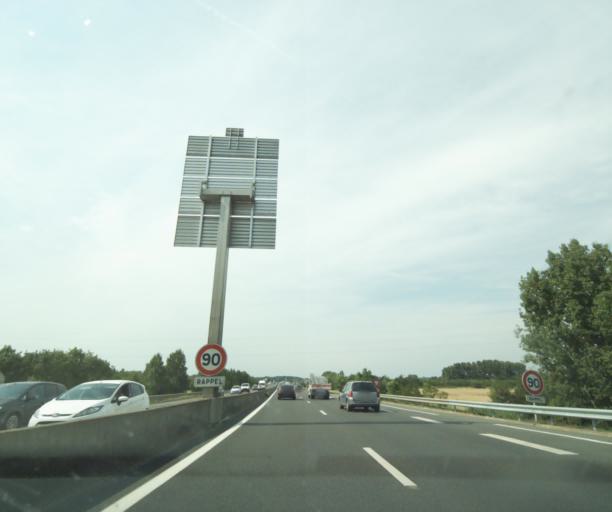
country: FR
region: Centre
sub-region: Departement d'Indre-et-Loire
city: Joue-les-Tours
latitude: 47.3702
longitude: 0.6545
